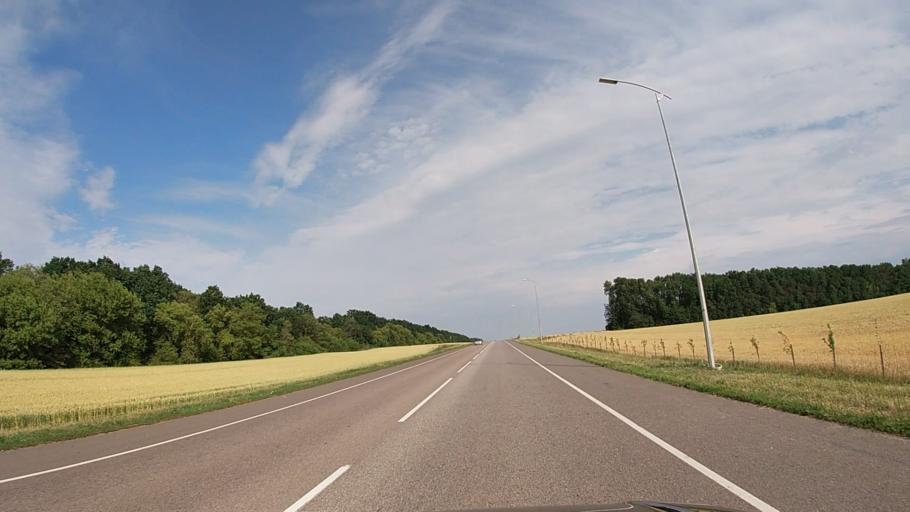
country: RU
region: Belgorod
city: Proletarskiy
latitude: 50.8240
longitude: 35.7850
